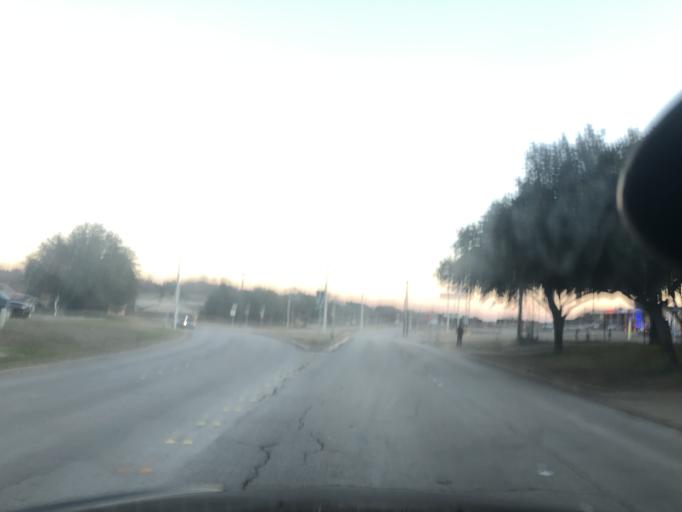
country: US
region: Texas
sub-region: Tarrant County
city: White Settlement
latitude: 32.7301
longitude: -97.4677
